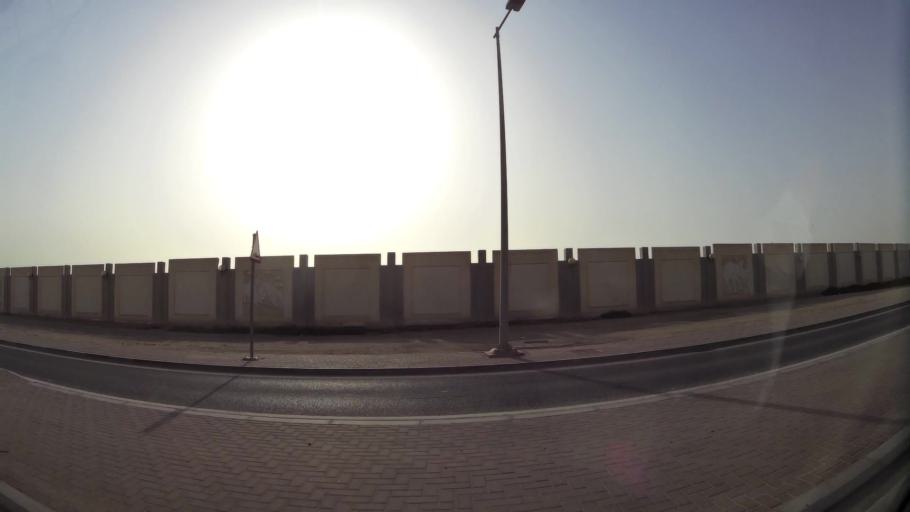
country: QA
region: Baladiyat ar Rayyan
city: Ar Rayyan
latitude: 25.2499
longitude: 51.4383
